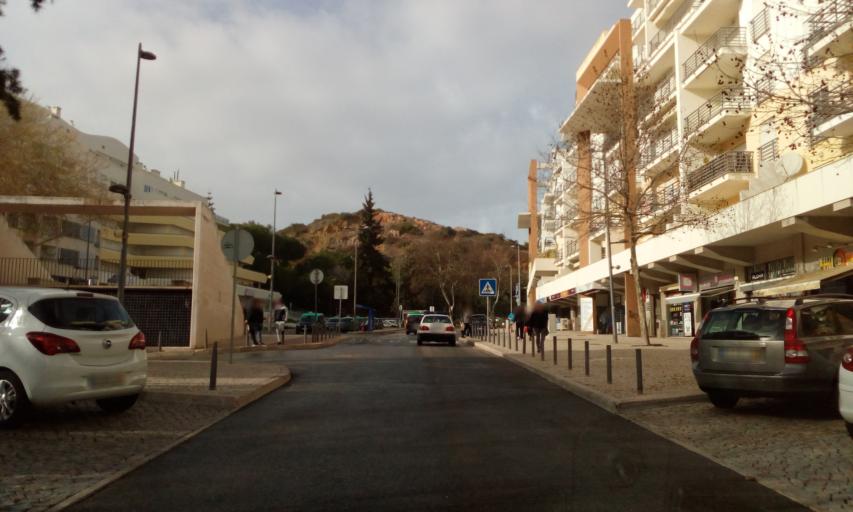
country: PT
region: Faro
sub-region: Albufeira
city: Albufeira
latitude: 37.0911
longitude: -8.2545
